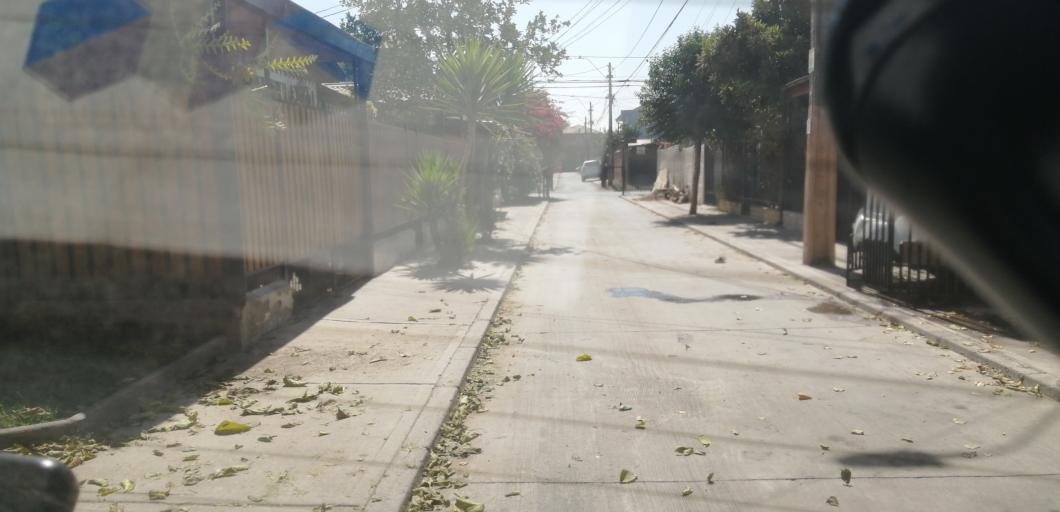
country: CL
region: Santiago Metropolitan
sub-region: Provincia de Santiago
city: Lo Prado
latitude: -33.4648
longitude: -70.7404
